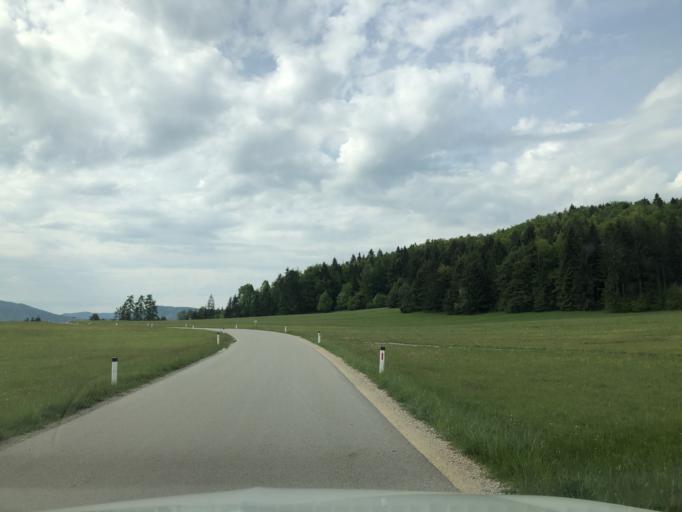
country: SI
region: Bloke
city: Nova Vas
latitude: 45.7863
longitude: 14.4991
